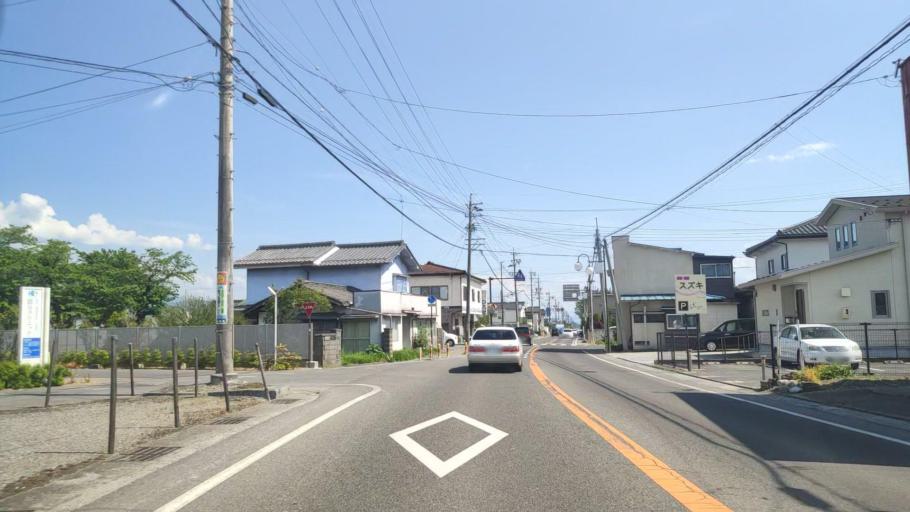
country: JP
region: Nagano
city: Hotaka
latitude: 36.3722
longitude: 137.8741
